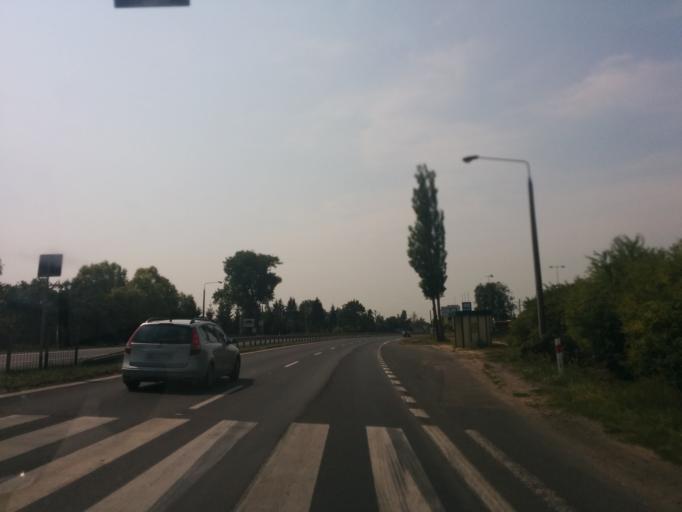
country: PL
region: Masovian Voivodeship
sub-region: Powiat pruszkowski
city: Nadarzyn
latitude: 52.0786
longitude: 20.7862
